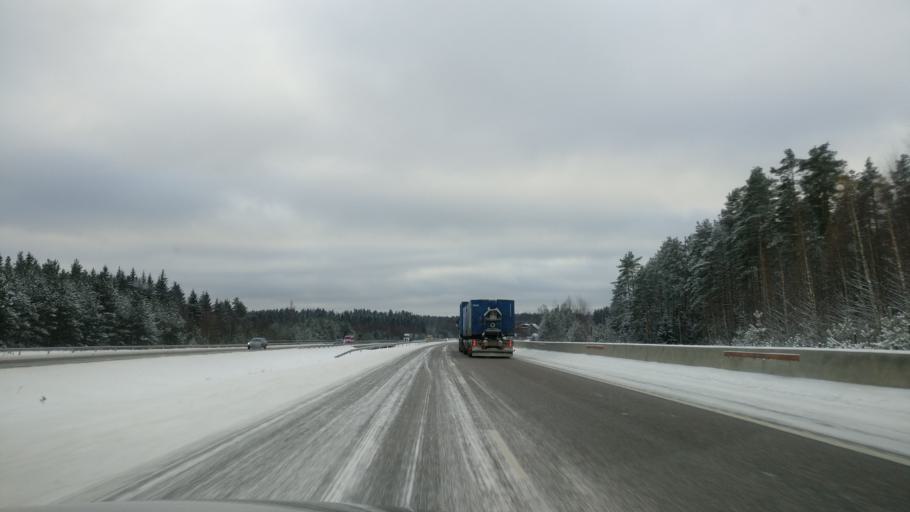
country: FI
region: Paijanne Tavastia
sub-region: Lahti
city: Nastola
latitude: 61.1029
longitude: 25.9115
